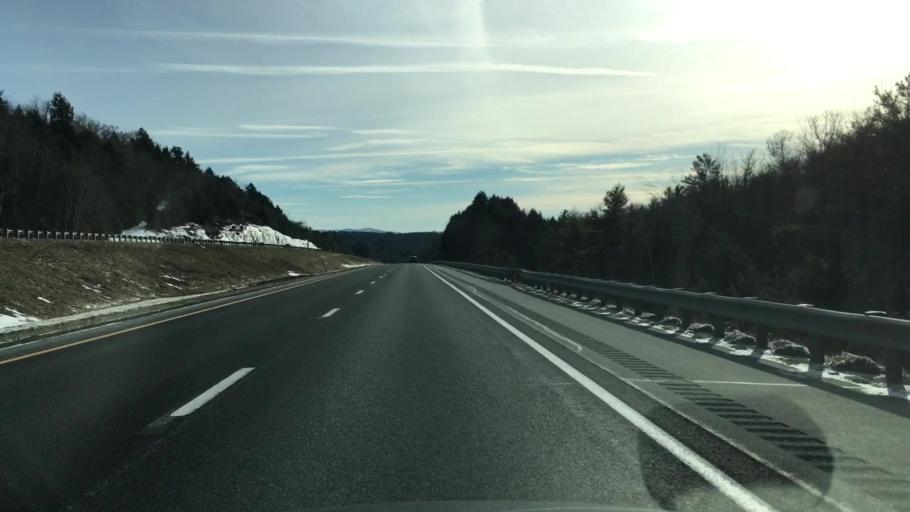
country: US
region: New Hampshire
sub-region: Sullivan County
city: Grantham
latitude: 43.5514
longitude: -72.1407
